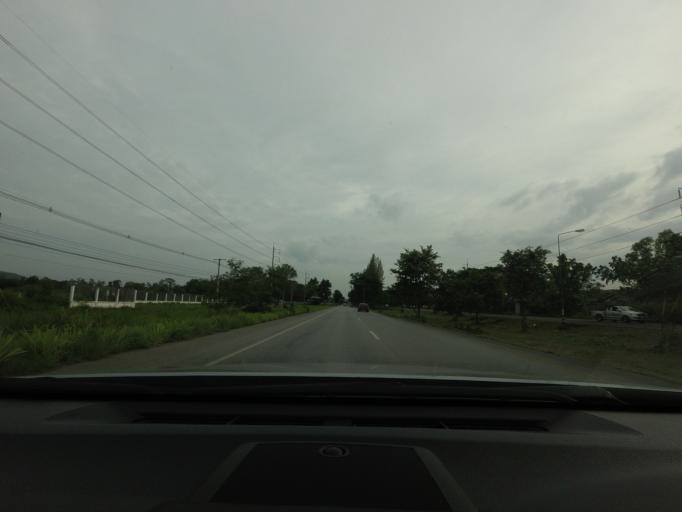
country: TH
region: Prachuap Khiri Khan
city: Hua Hin
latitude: 12.6474
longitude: 99.8677
